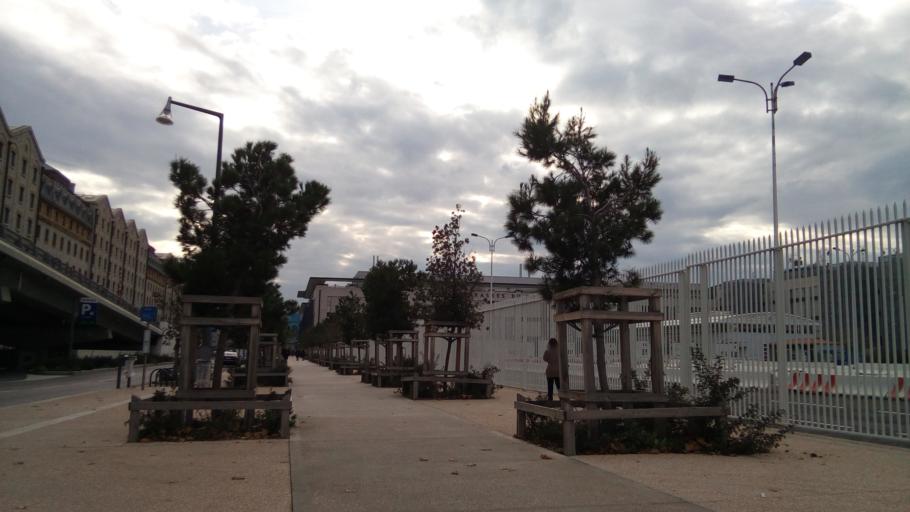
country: FR
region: Provence-Alpes-Cote d'Azur
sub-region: Departement des Bouches-du-Rhone
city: Marseille 03
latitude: 43.3112
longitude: 5.3678
